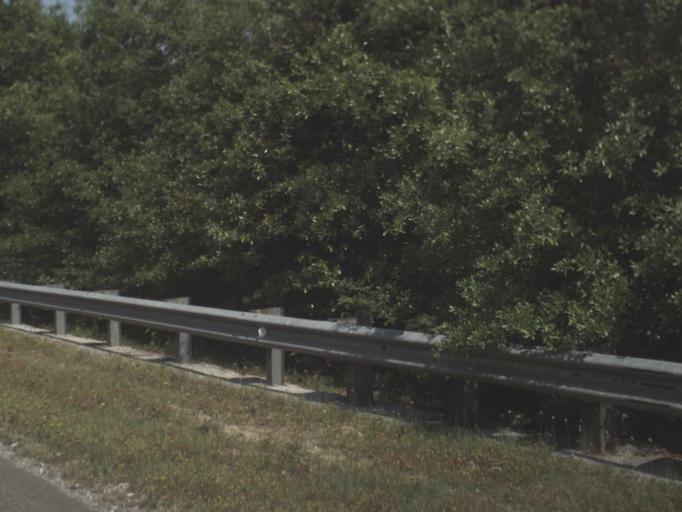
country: US
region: Florida
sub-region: Escambia County
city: Myrtle Grove
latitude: 30.4207
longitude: -87.3508
